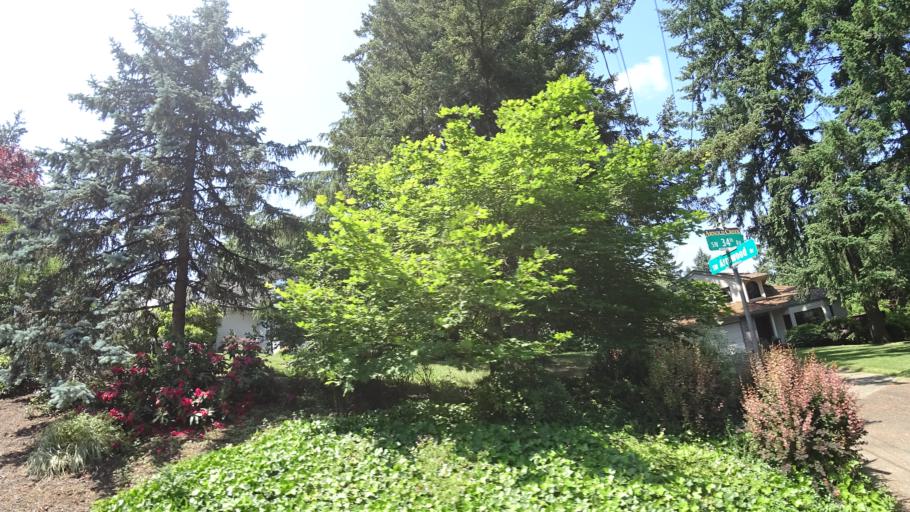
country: US
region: Oregon
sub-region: Clackamas County
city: Lake Oswego
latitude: 45.4362
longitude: -122.7117
